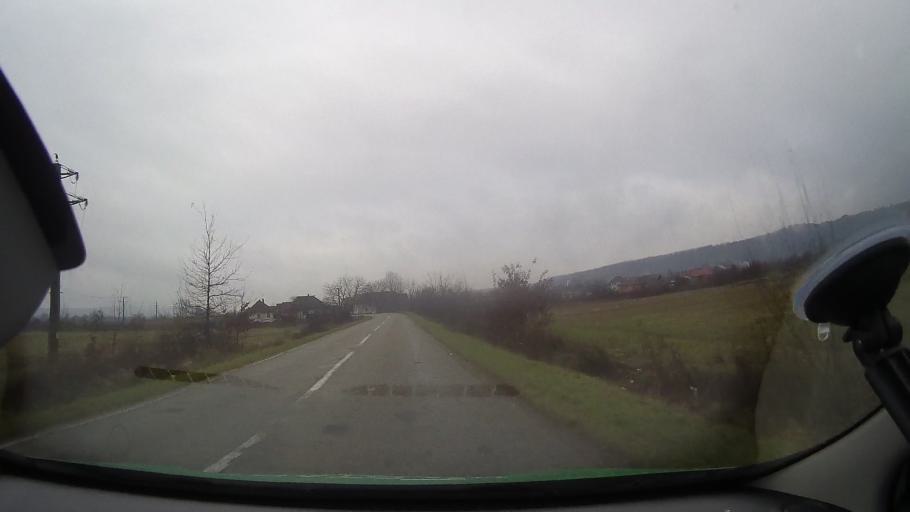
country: RO
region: Arad
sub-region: Comuna Ignesti
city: Ignesti
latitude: 46.4065
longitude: 22.2043
